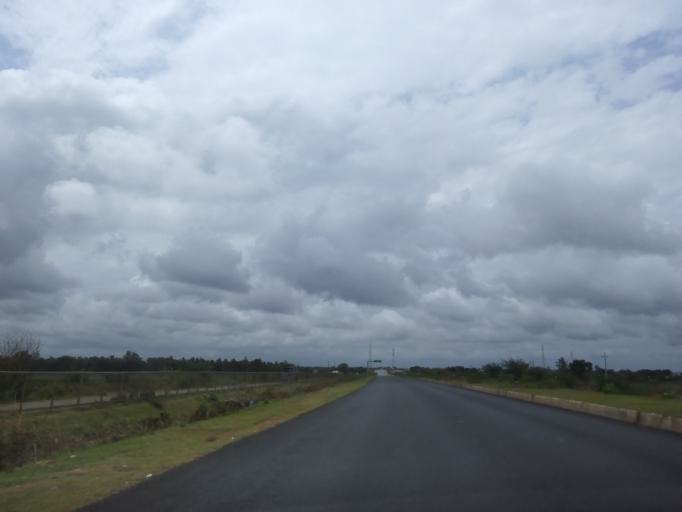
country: IN
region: Karnataka
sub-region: Haveri
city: Byadgi
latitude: 14.6852
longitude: 75.5395
